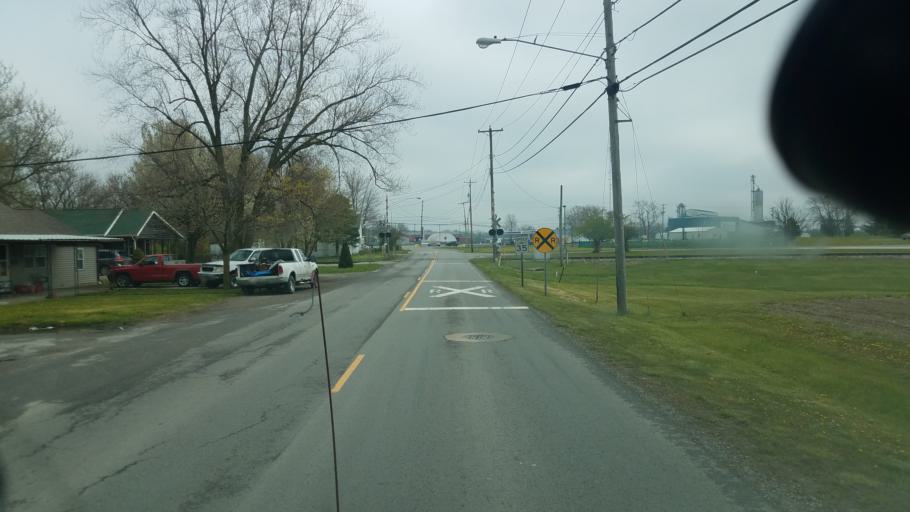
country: US
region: Ohio
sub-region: Hardin County
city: Kenton
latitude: 40.6341
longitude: -83.6048
